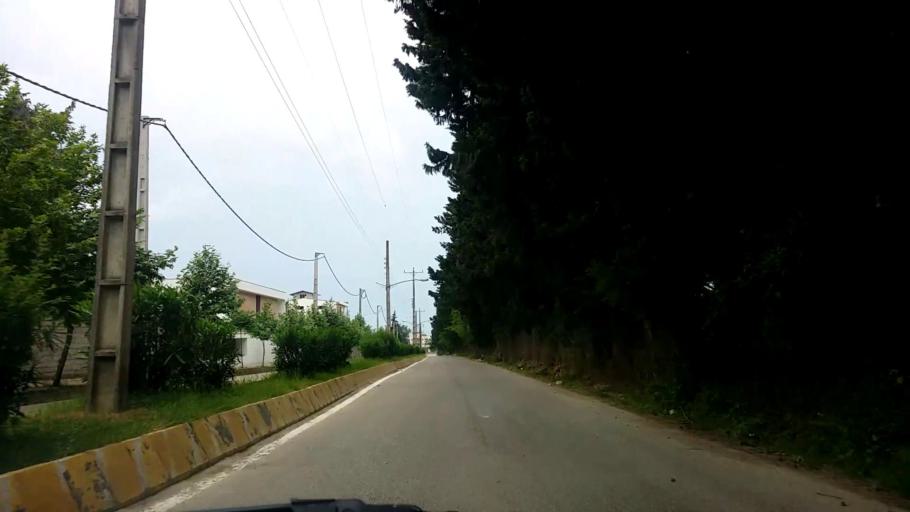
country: IR
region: Mazandaran
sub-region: Nowshahr
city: Nowshahr
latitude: 36.6339
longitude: 51.5026
